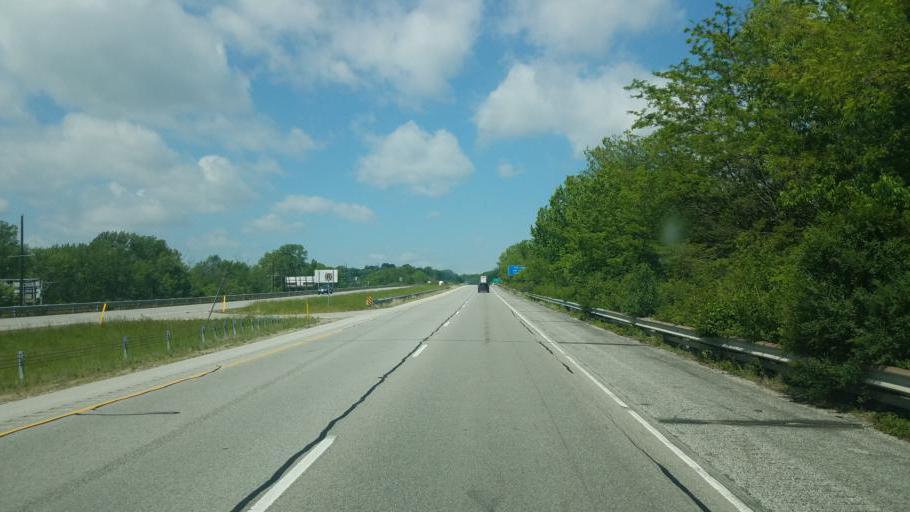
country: US
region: Indiana
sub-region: Vigo County
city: West Terre Haute
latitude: 39.4488
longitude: -87.4561
